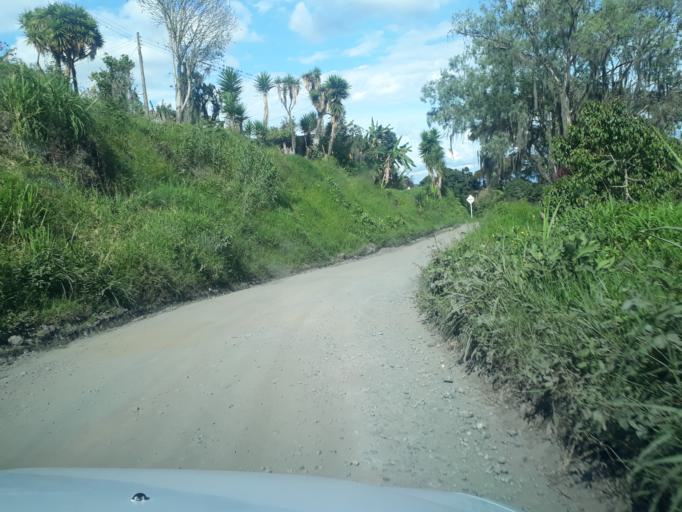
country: CO
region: Santander
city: Velez
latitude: 6.0423
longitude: -73.6531
